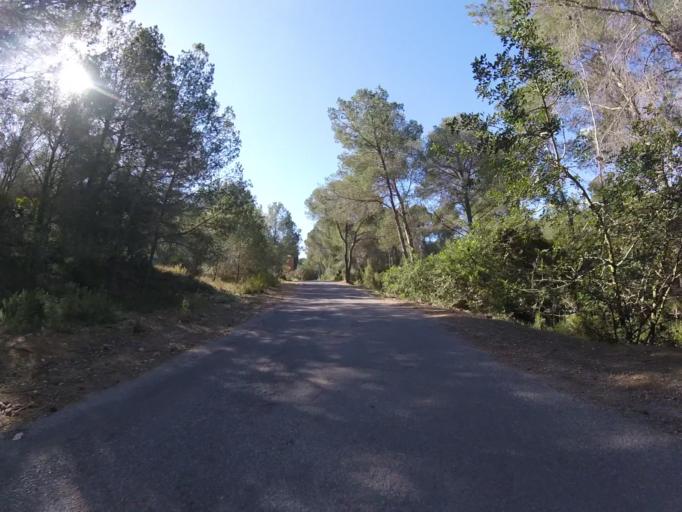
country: ES
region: Valencia
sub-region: Provincia de Castello
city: Orpesa/Oropesa del Mar
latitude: 40.0770
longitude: 0.1175
